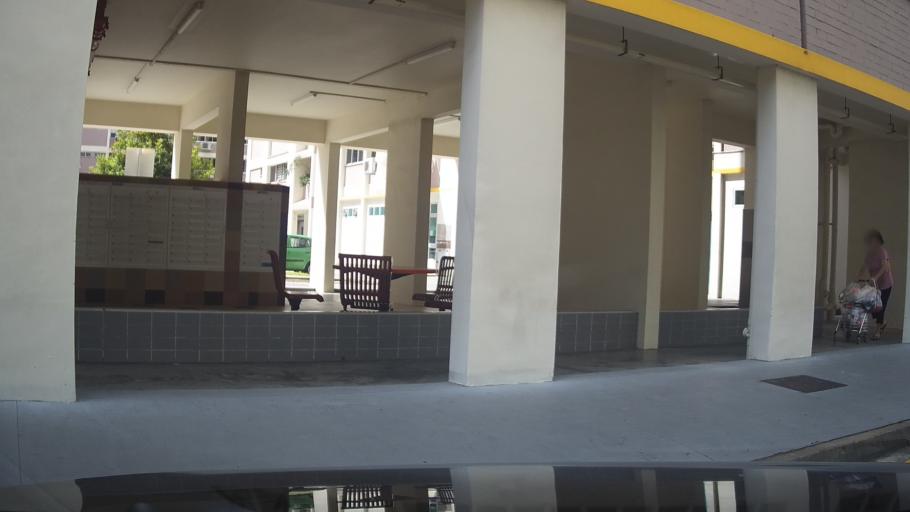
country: SG
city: Singapore
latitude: 1.3322
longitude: 103.8569
